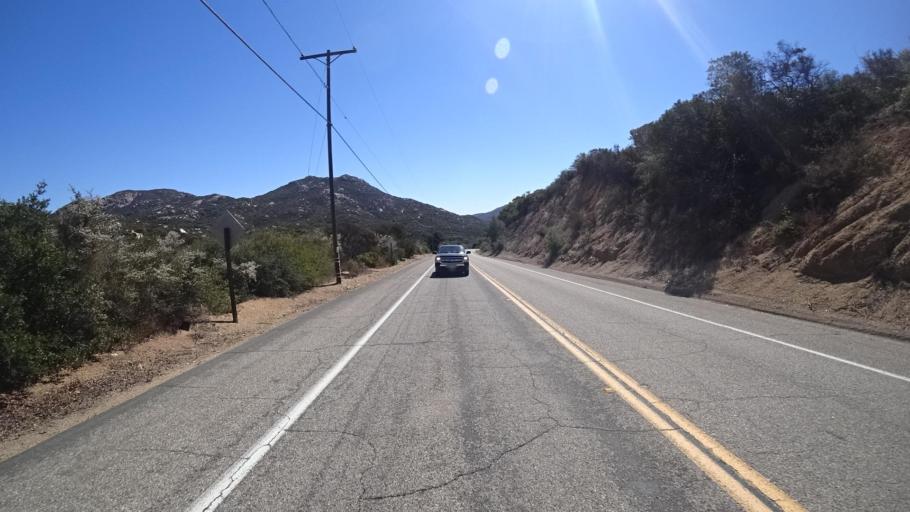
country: US
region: California
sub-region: San Diego County
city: Alpine
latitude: 32.7249
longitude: -116.7631
